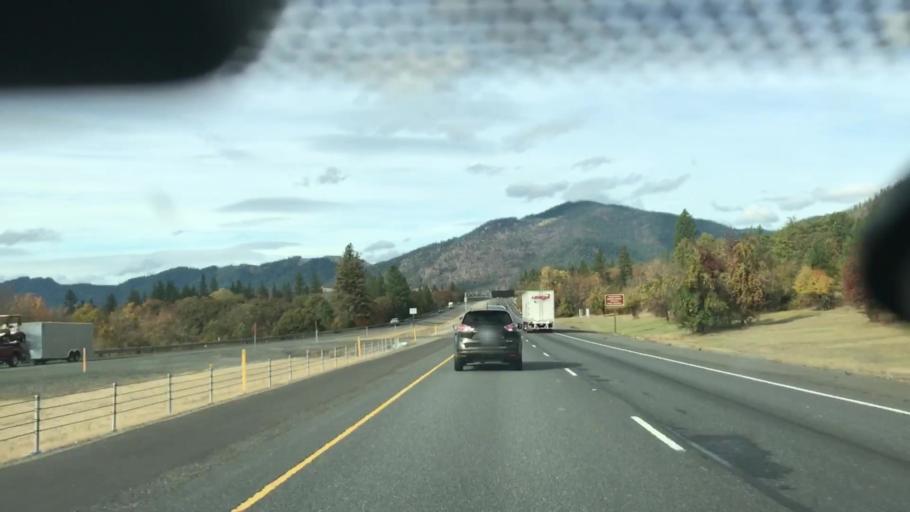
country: US
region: Oregon
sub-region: Josephine County
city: Merlin
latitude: 42.5341
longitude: -123.3695
